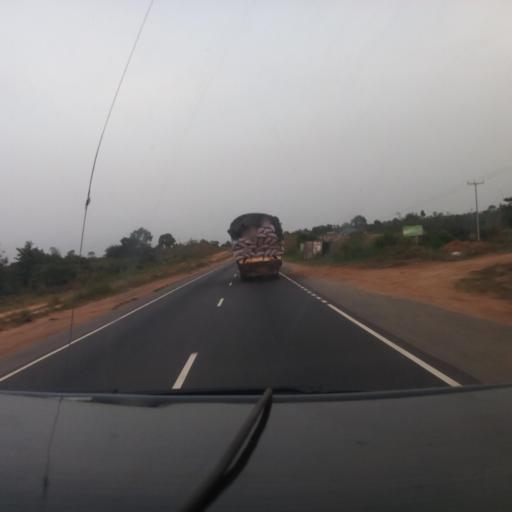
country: GH
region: Eastern
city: Nsawam
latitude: 5.8862
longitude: -0.3783
